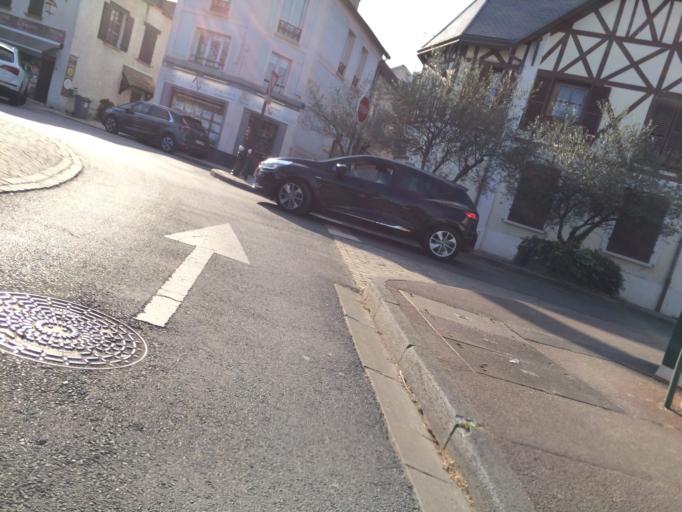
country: FR
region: Ile-de-France
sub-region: Departement de l'Essonne
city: Verrieres-le-Buisson
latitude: 48.7465
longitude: 2.2647
